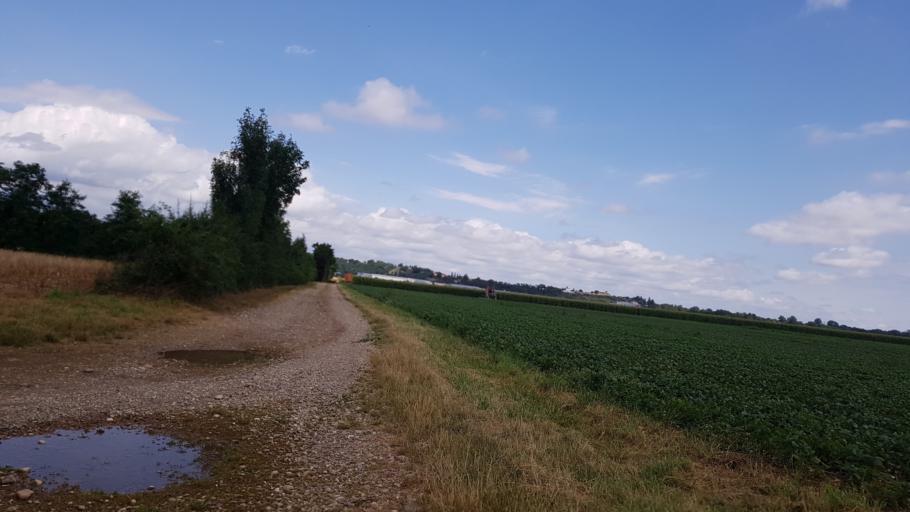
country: FR
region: Rhone-Alpes
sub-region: Departement du Rhone
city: Pusignan
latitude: 45.7333
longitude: 5.0666
